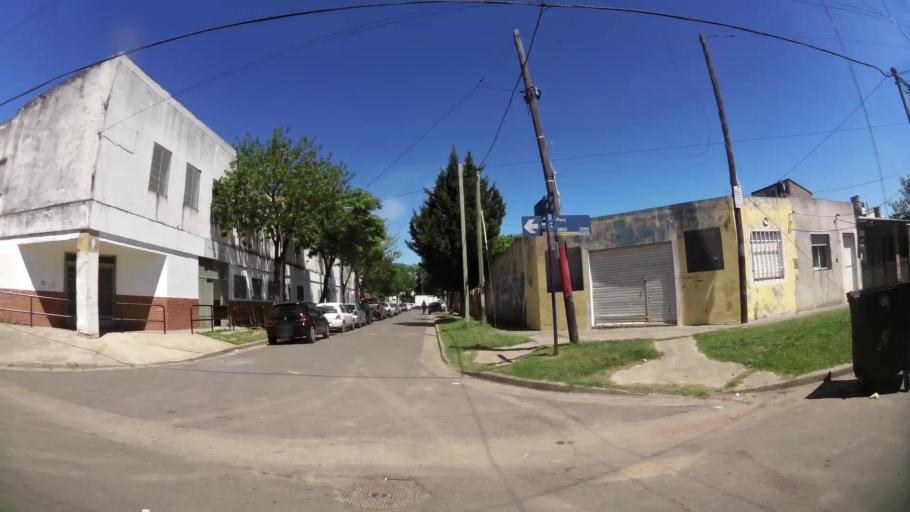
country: AR
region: Santa Fe
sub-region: Departamento de Rosario
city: Rosario
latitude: -32.9527
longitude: -60.7109
